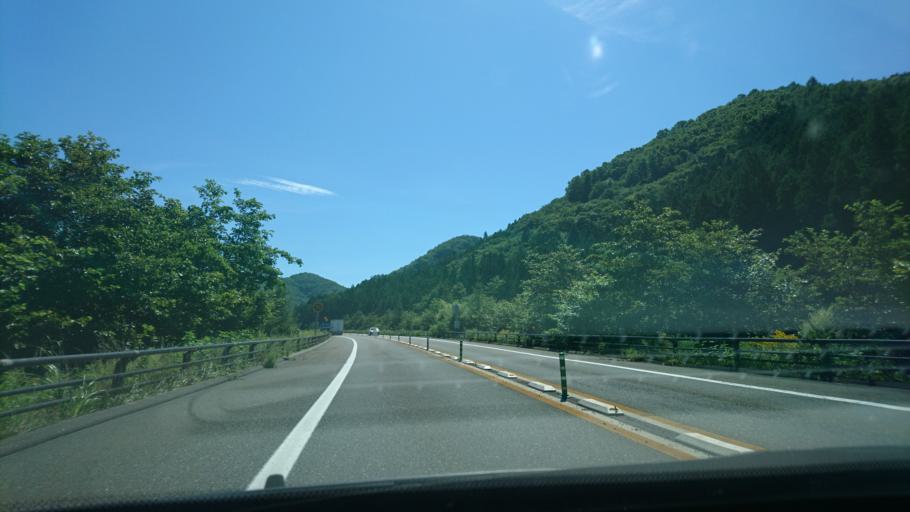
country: JP
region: Iwate
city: Tono
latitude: 39.2603
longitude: 141.6175
